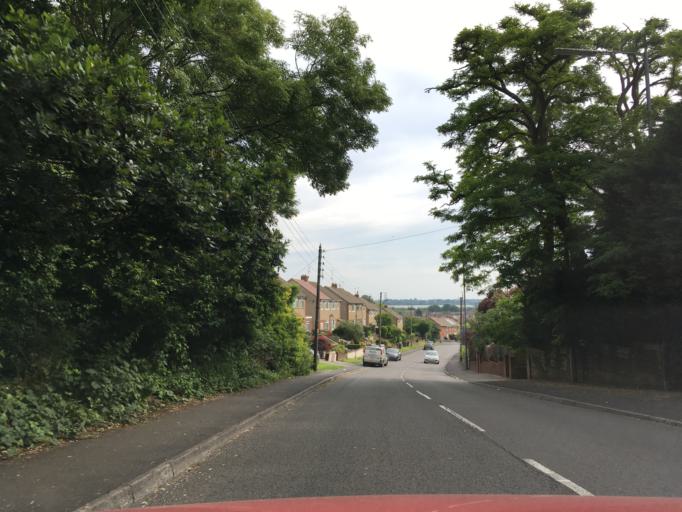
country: GB
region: England
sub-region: South Gloucestershire
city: Mangotsfield
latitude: 51.4922
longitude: -2.4924
